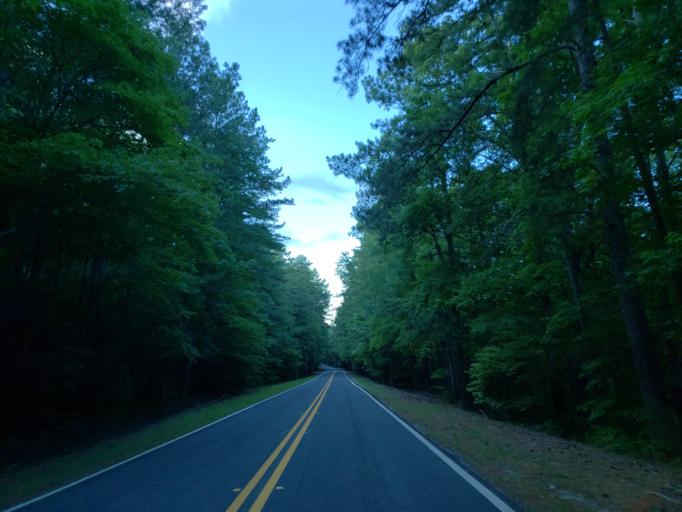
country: US
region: Georgia
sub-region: Bartow County
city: Emerson
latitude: 34.1751
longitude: -84.7363
